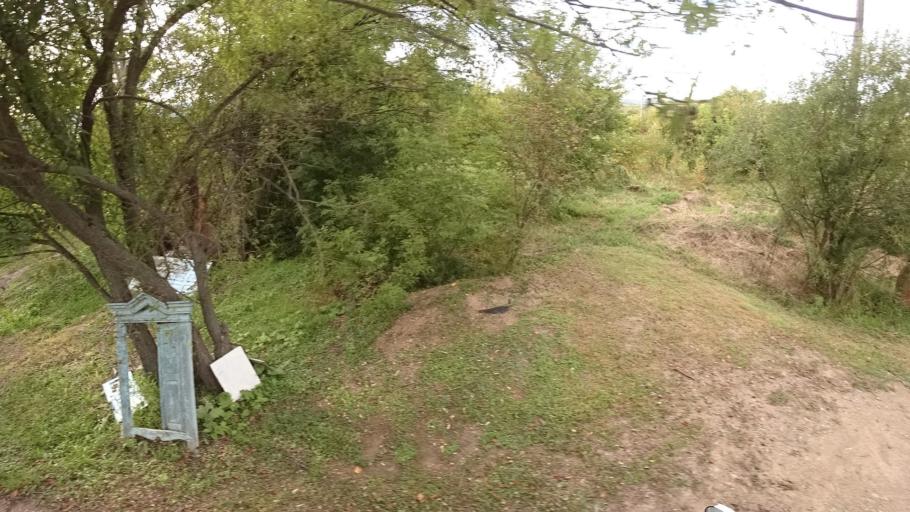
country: RU
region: Primorskiy
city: Yakovlevka
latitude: 44.4181
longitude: 133.4556
